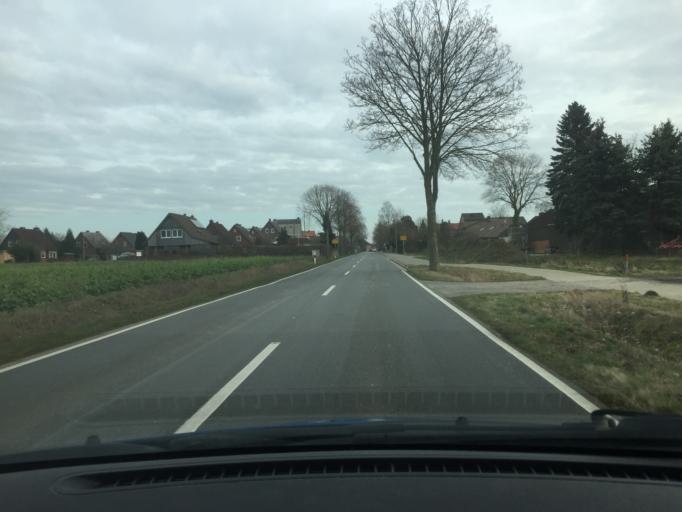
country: DE
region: Lower Saxony
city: Rosche
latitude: 52.9885
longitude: 10.7434
